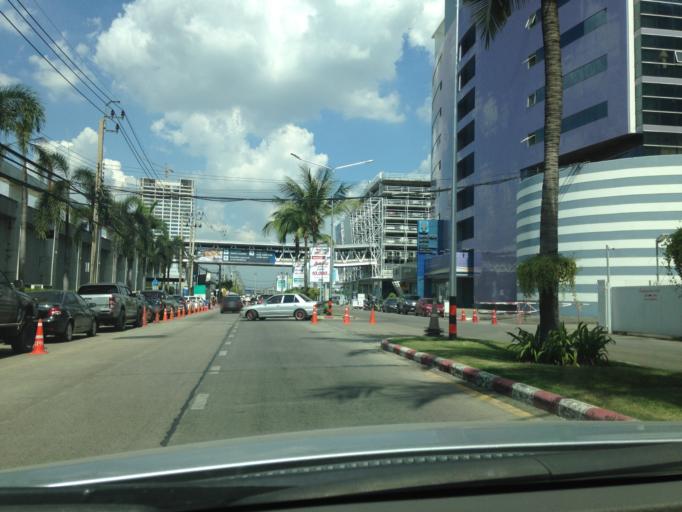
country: TH
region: Bangkok
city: Lak Si
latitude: 13.9108
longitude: 100.5492
